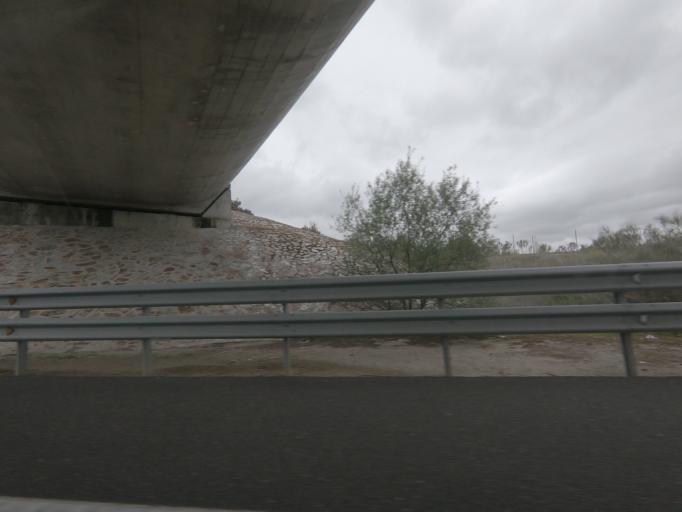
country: ES
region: Extremadura
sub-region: Provincia de Caceres
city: Mirabel
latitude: 39.9221
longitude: -6.2371
